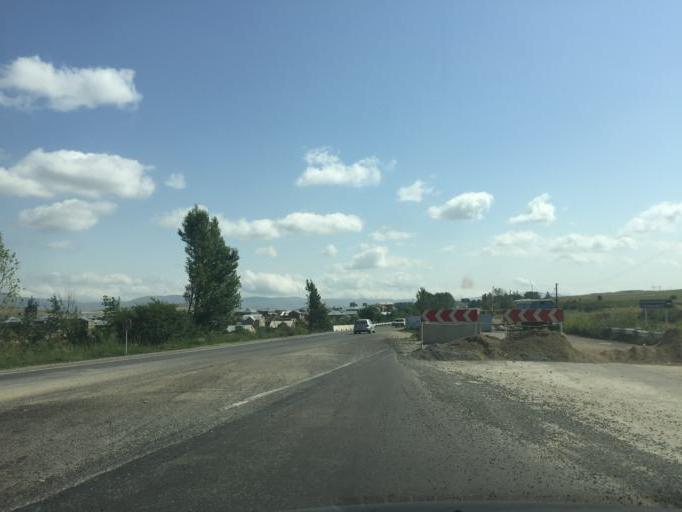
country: AM
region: Kotayk'i Marz
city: Hrazdan
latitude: 40.4823
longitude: 44.7625
